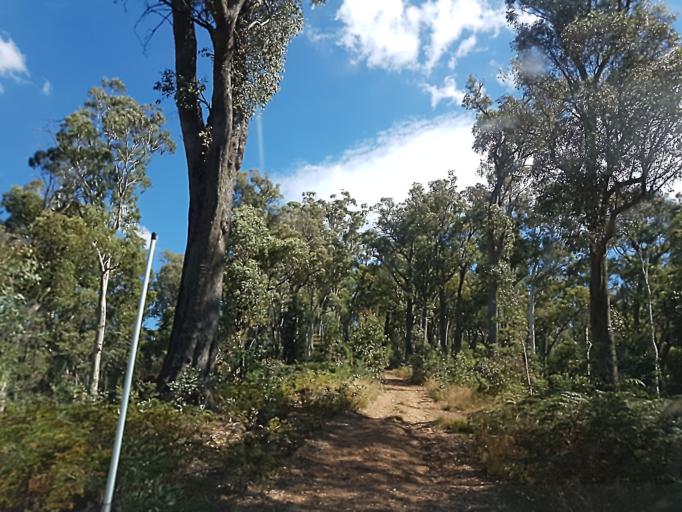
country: AU
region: Victoria
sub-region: Alpine
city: Mount Beauty
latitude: -36.8807
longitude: 147.0251
